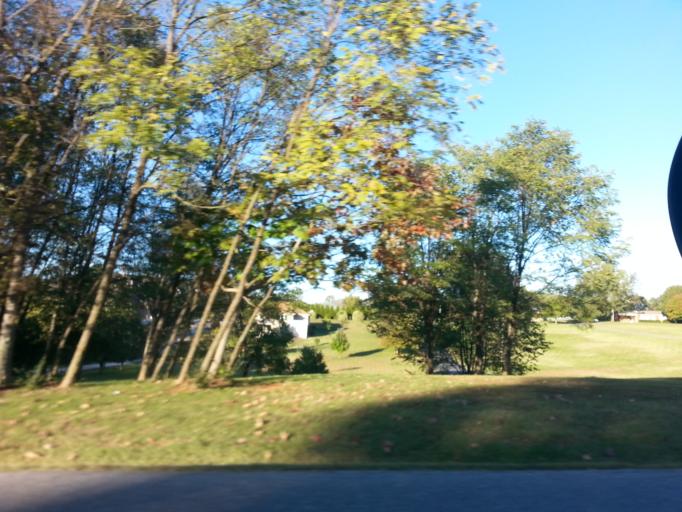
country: US
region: Tennessee
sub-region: Blount County
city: Eagleton Village
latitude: 35.7726
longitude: -83.9369
